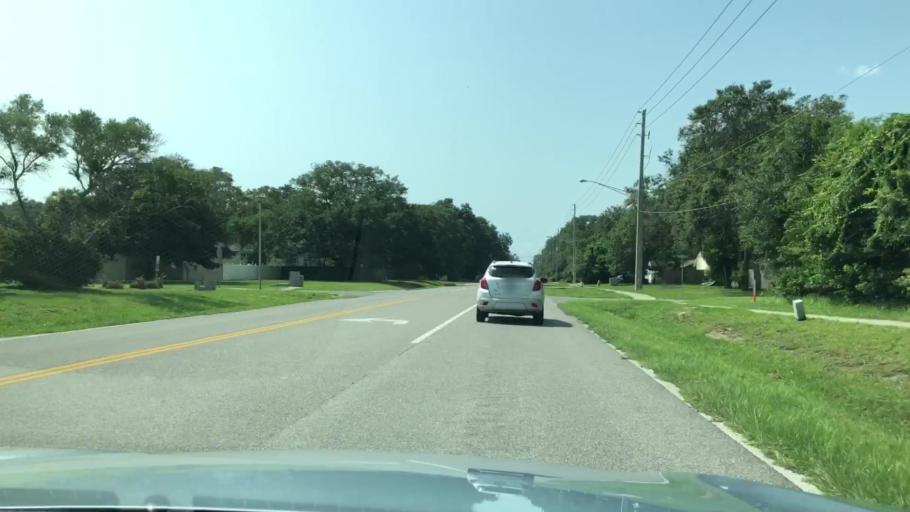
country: US
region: Florida
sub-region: Duval County
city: Neptune Beach
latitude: 30.3202
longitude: -81.4085
